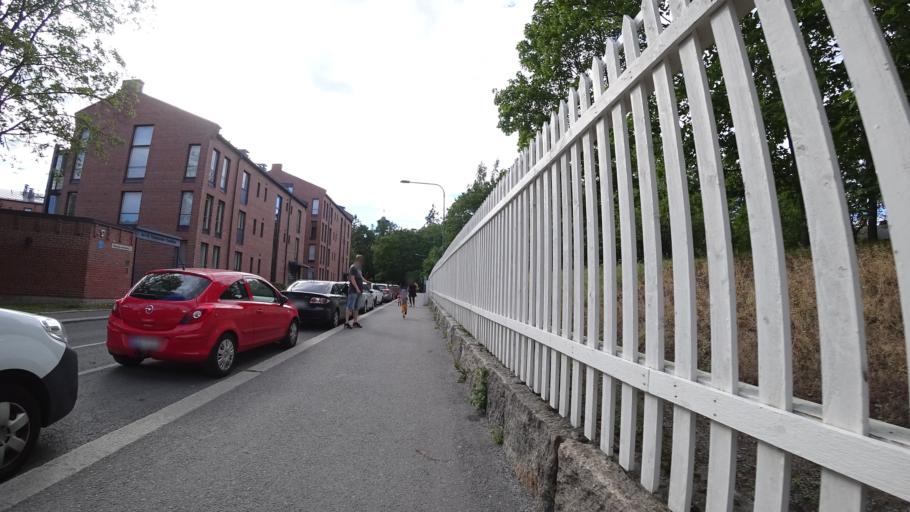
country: FI
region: Pirkanmaa
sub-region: Tampere
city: Tampere
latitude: 61.5027
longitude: 23.7553
